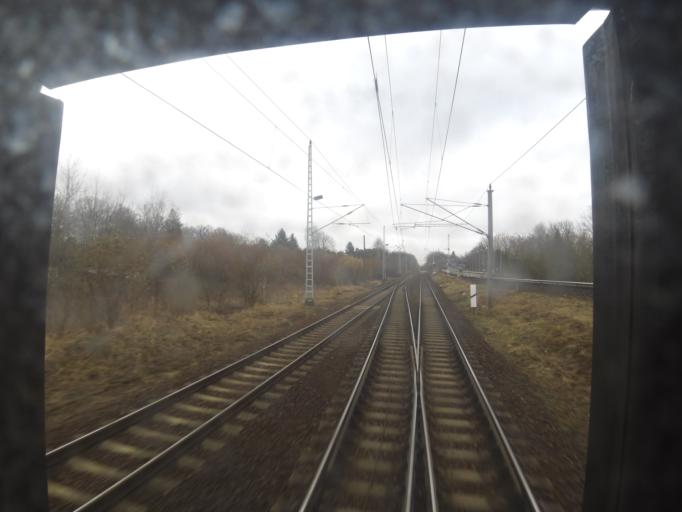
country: DE
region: Brandenburg
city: Rangsdorf
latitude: 52.3400
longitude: 13.4152
